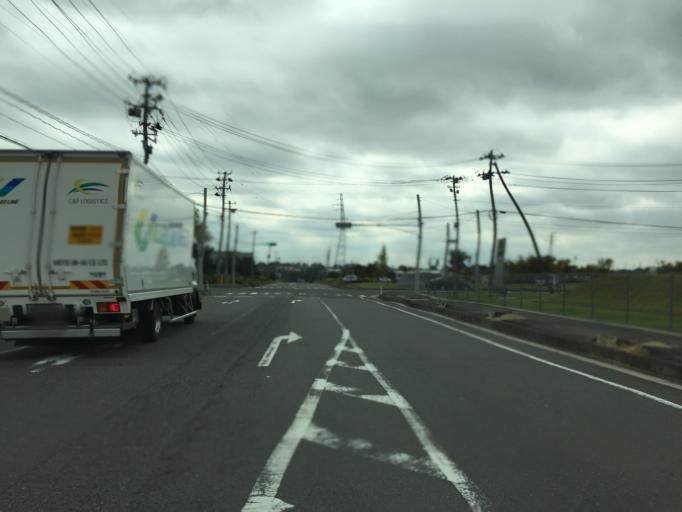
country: JP
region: Fukushima
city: Motomiya
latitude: 37.4797
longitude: 140.3739
